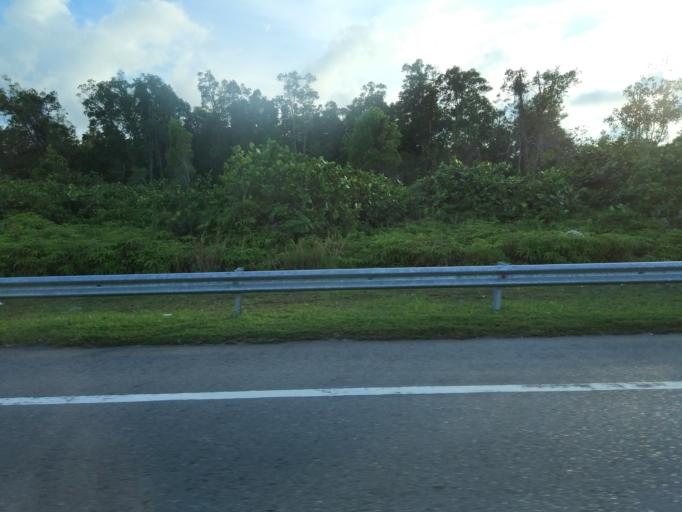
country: BN
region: Tutong
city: Tutong
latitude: 4.7776
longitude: 114.6542
